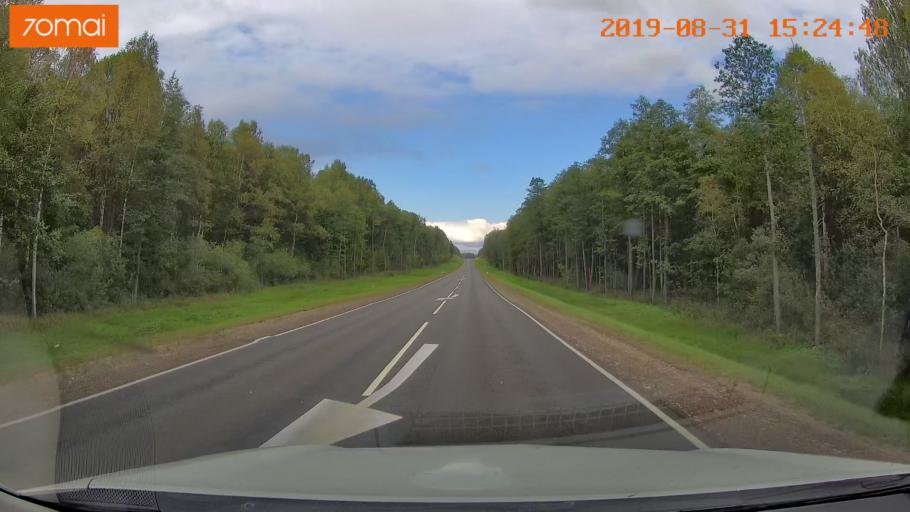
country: RU
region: Kaluga
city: Baryatino
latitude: 54.5325
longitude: 34.5099
